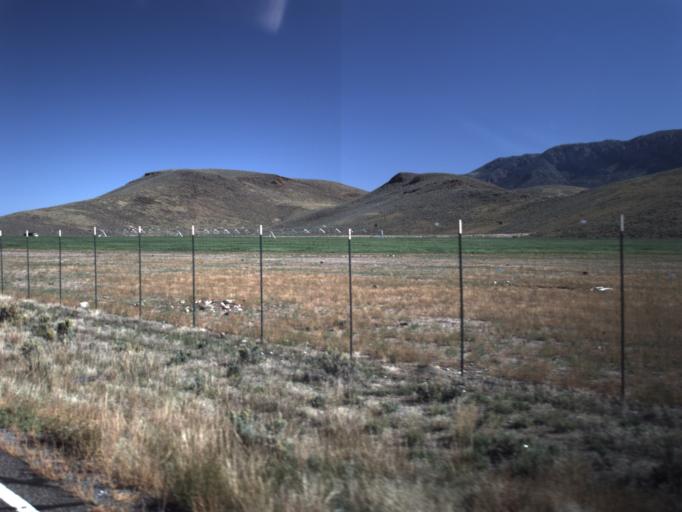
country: US
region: Utah
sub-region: Piute County
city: Junction
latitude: 38.2644
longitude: -111.9864
